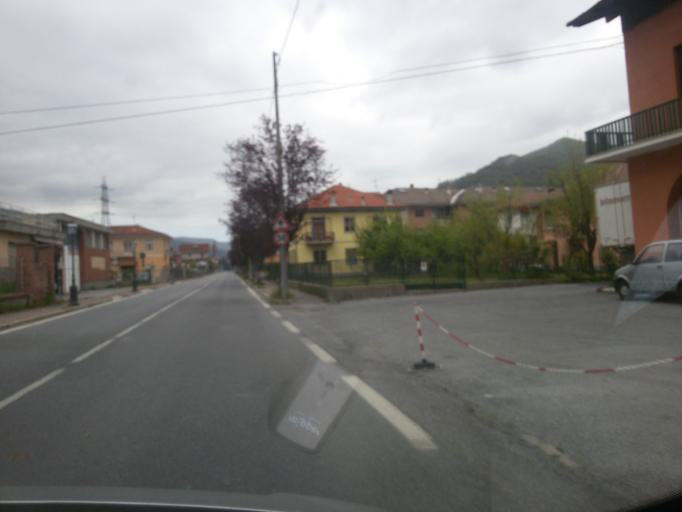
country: IT
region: Piedmont
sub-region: Provincia di Cuneo
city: Garessio
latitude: 44.2063
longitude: 8.0148
